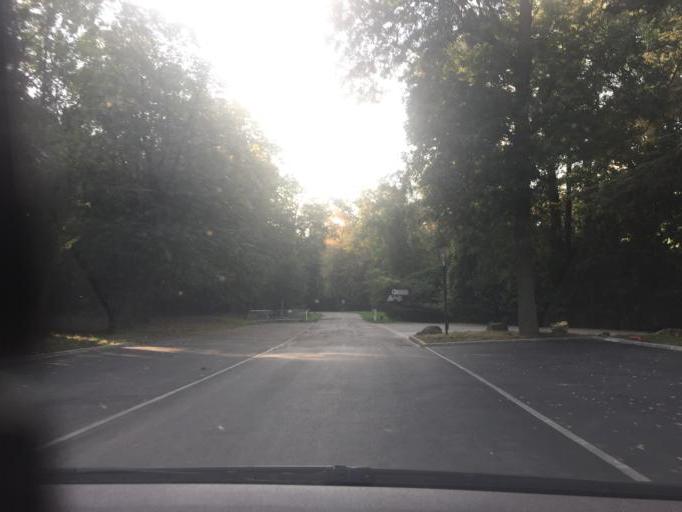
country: FR
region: Ile-de-France
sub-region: Departement des Yvelines
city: Jouy-en-Josas
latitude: 48.7563
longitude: 2.1619
